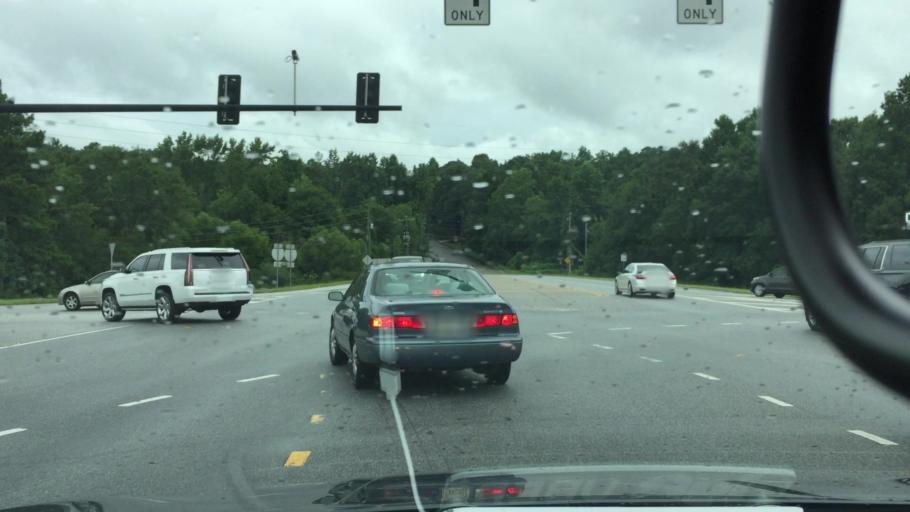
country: US
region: Alabama
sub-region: Lee County
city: Auburn
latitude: 32.6042
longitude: -85.4278
